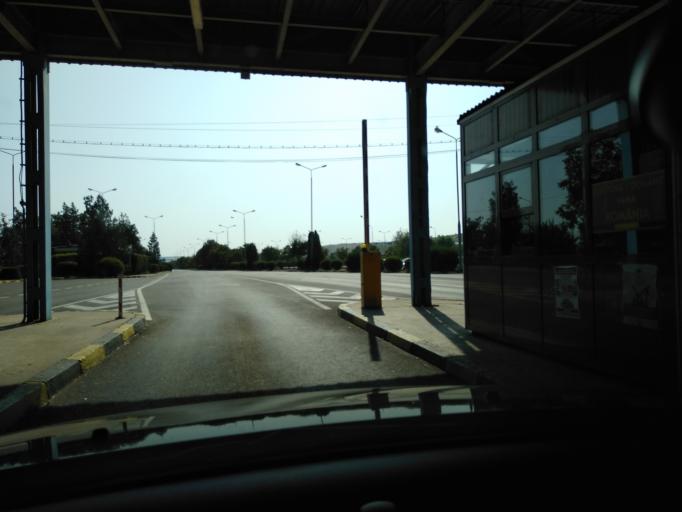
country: RO
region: Vaslui
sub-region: Comuna Dranceni
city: Rasesti
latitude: 46.7869
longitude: 28.1430
